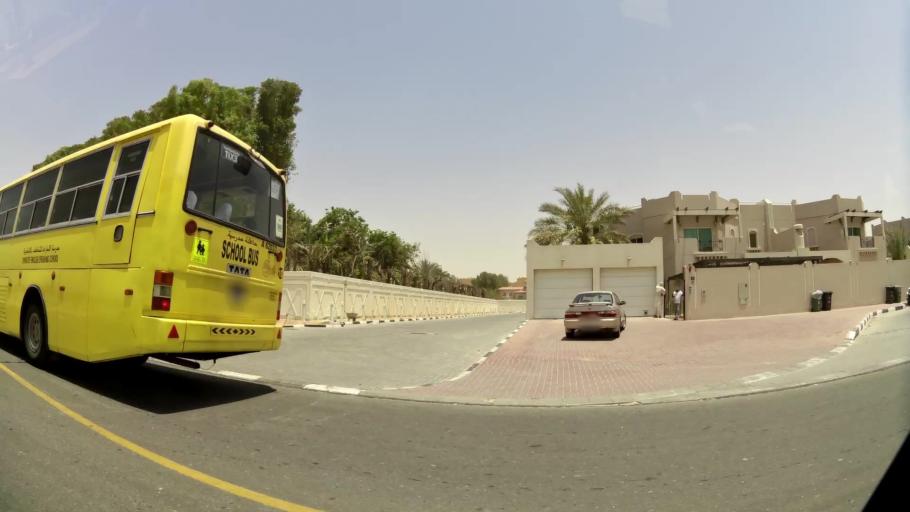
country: AE
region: Dubai
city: Dubai
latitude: 25.1797
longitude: 55.2442
